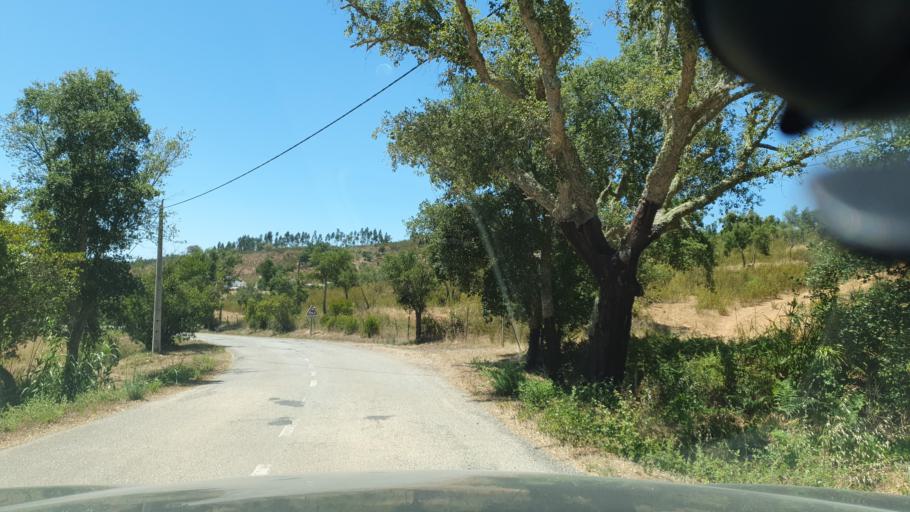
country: PT
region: Beja
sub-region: Odemira
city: Odemira
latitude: 37.6132
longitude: -8.5067
